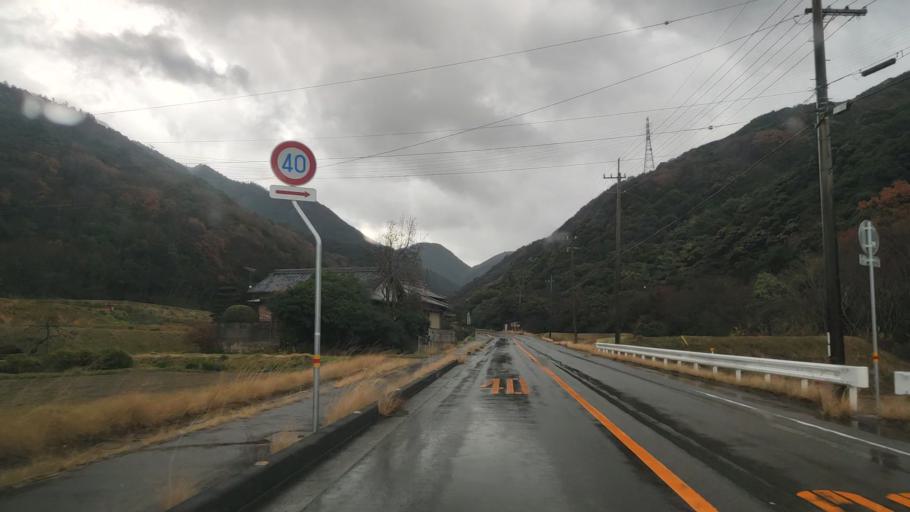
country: JP
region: Tokushima
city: Kamojimacho-jogejima
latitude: 34.1932
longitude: 134.3338
